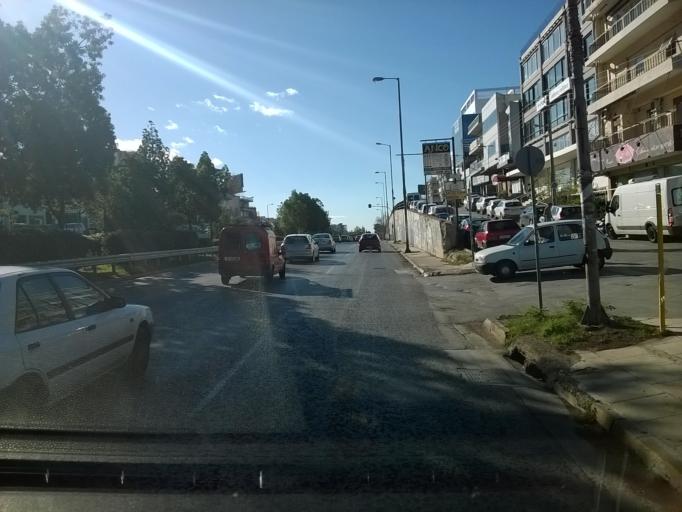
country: GR
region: Attica
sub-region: Nomarchia Athinas
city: Agios Dimitrios
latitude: 37.9330
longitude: 23.7443
